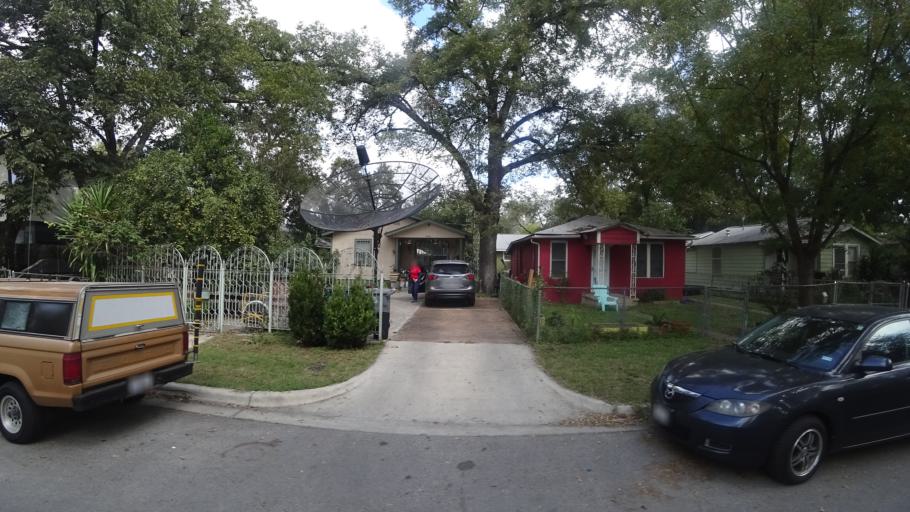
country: US
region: Texas
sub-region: Travis County
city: Austin
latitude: 30.2561
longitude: -97.7156
